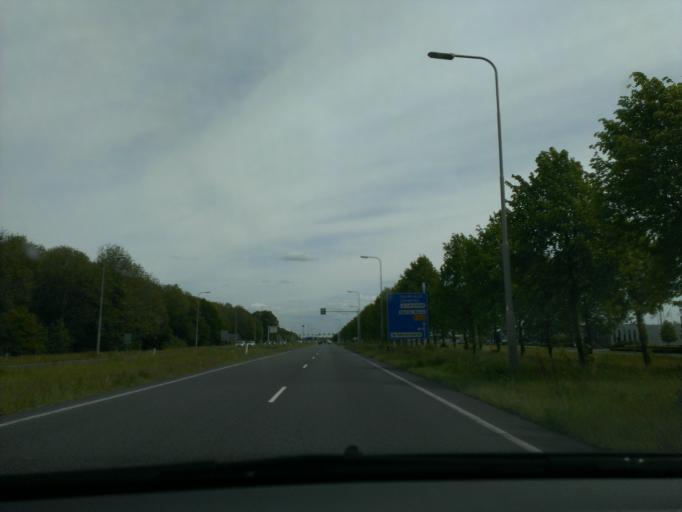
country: NL
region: Flevoland
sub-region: Gemeente Lelystad
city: Lelystad
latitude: 52.4768
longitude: 5.5084
